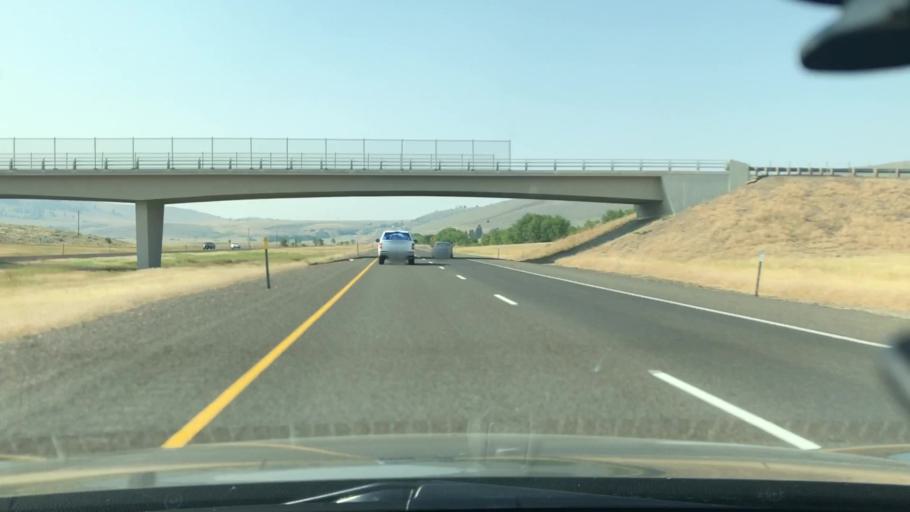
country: US
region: Oregon
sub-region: Union County
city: Union
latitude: 45.1234
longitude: -117.9623
